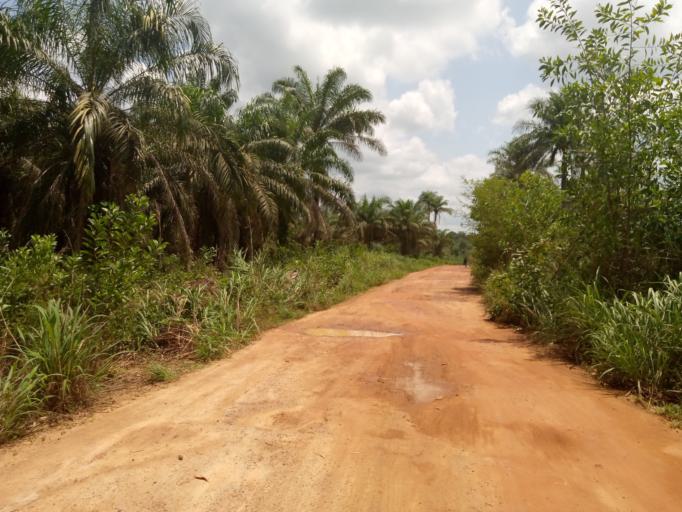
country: SL
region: Western Area
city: Waterloo
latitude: 8.3738
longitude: -12.9639
